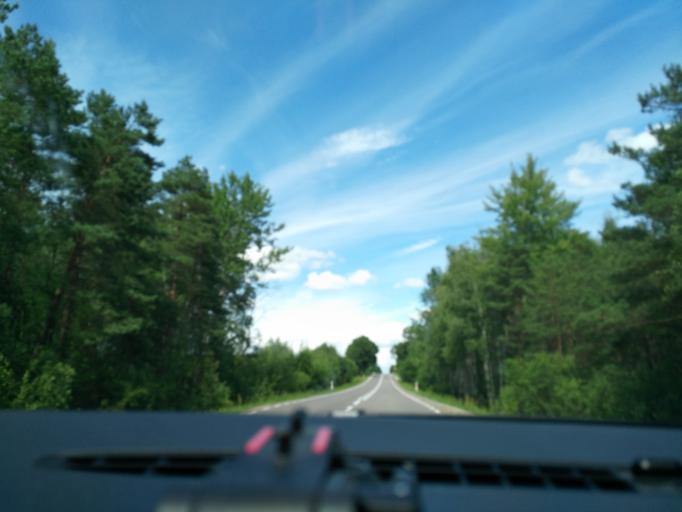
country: PL
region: Podlasie
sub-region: Powiat sejnenski
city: Sejny
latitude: 54.0222
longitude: 23.3416
